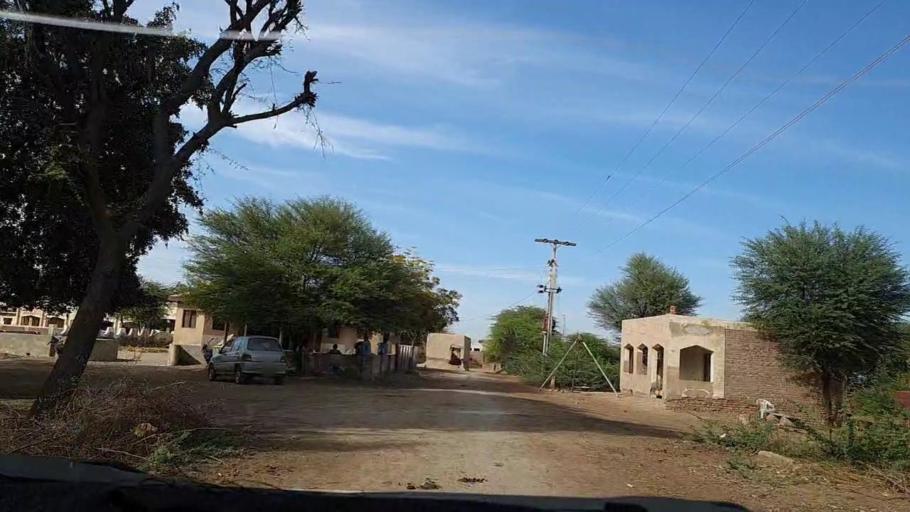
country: PK
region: Sindh
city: Dhoro Naro
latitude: 25.4781
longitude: 69.5352
